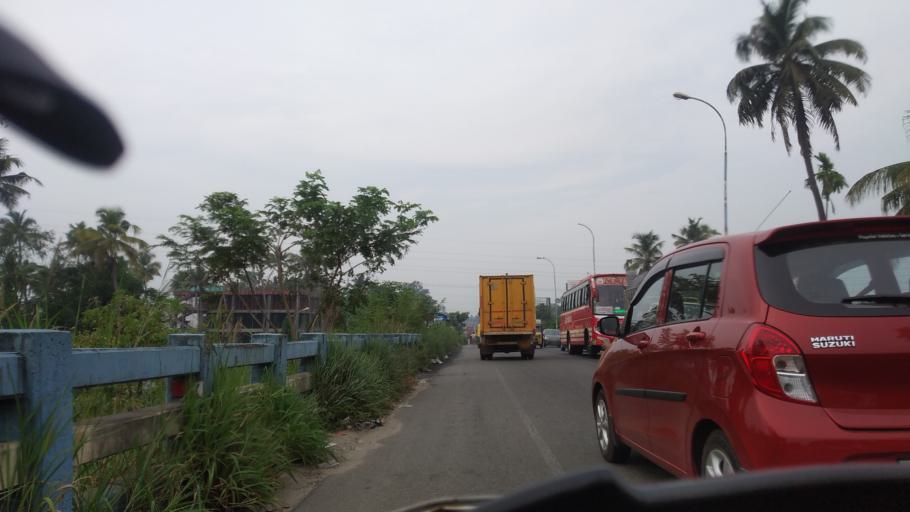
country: IN
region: Kerala
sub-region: Ernakulam
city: Elur
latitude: 10.0393
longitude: 76.3010
